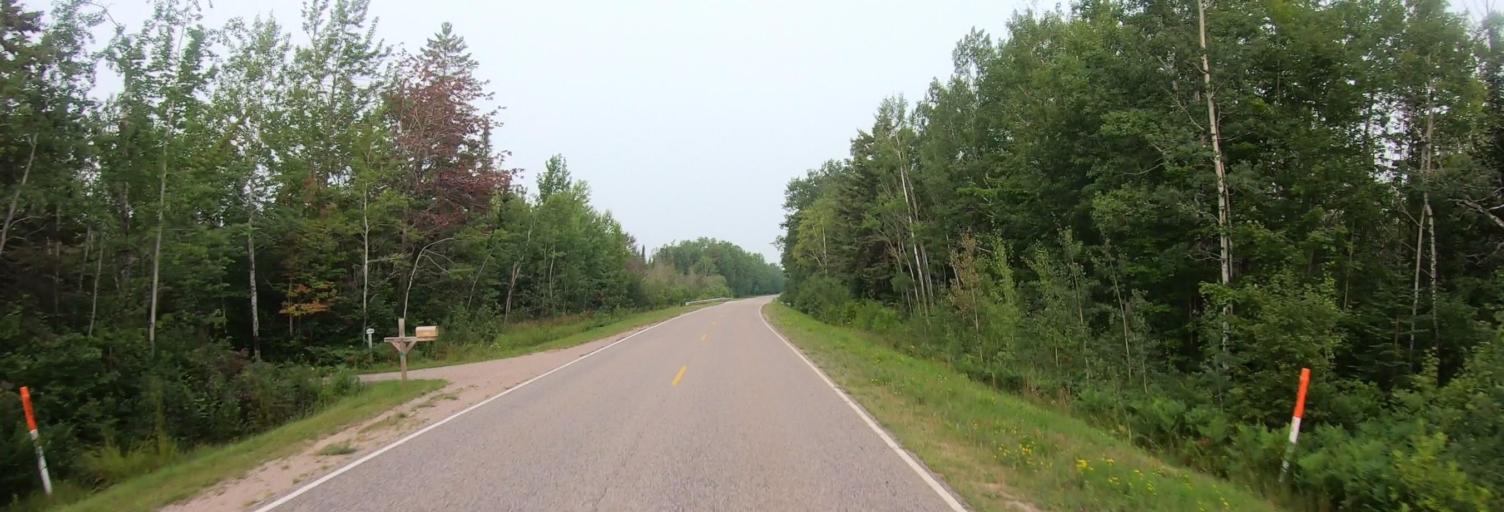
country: US
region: Michigan
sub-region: Chippewa County
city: Sault Ste. Marie
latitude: 46.4645
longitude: -84.8968
